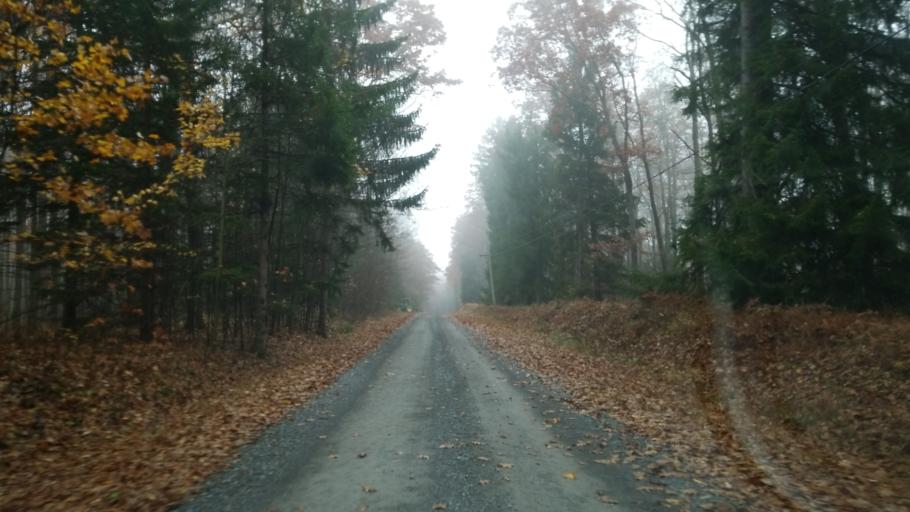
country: US
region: Pennsylvania
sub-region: Clearfield County
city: Clearfield
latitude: 41.1041
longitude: -78.5262
